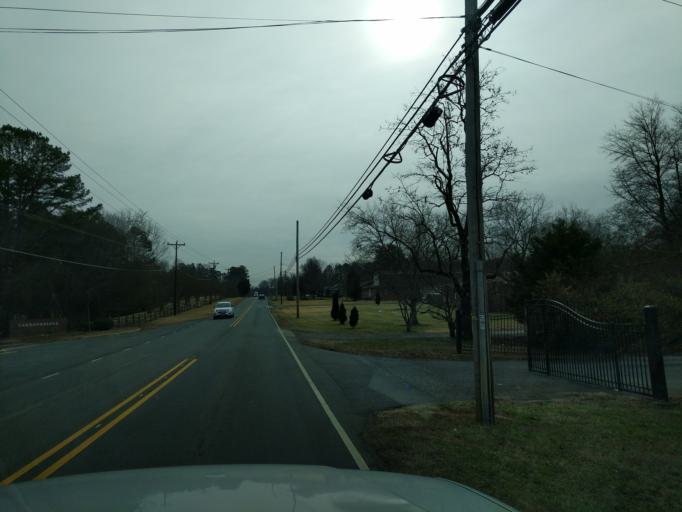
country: US
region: North Carolina
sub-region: Mecklenburg County
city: Charlotte
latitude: 35.3128
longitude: -80.8805
